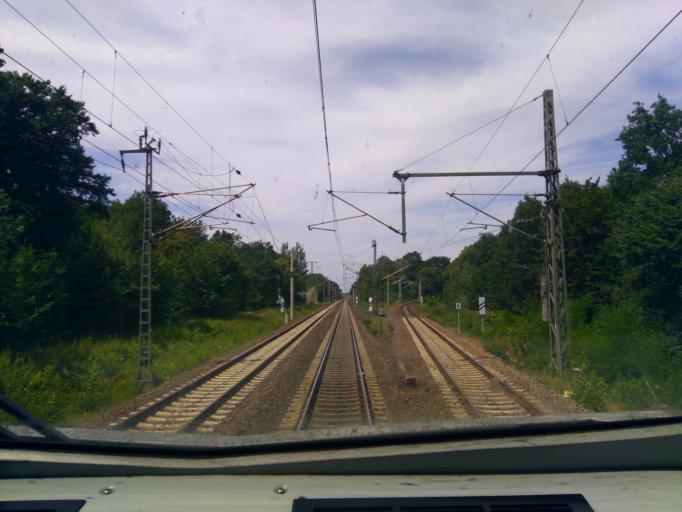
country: DE
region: Brandenburg
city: Brieselang
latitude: 52.5750
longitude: 13.0312
